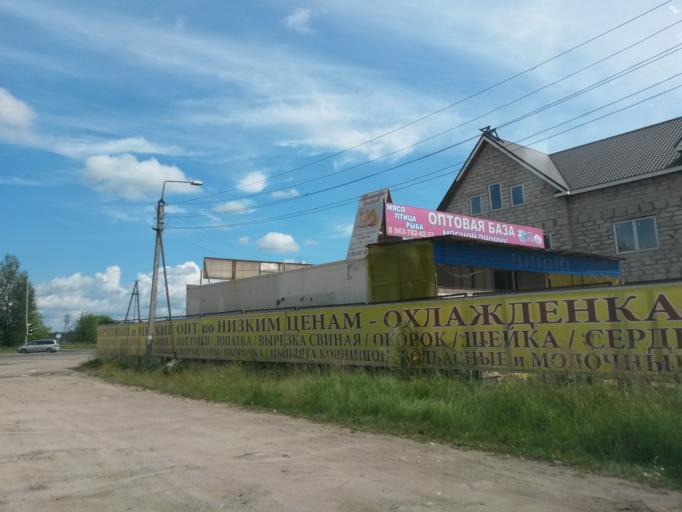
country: RU
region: Jaroslavl
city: Pereslavl'-Zalesskiy
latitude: 56.7813
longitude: 38.8820
